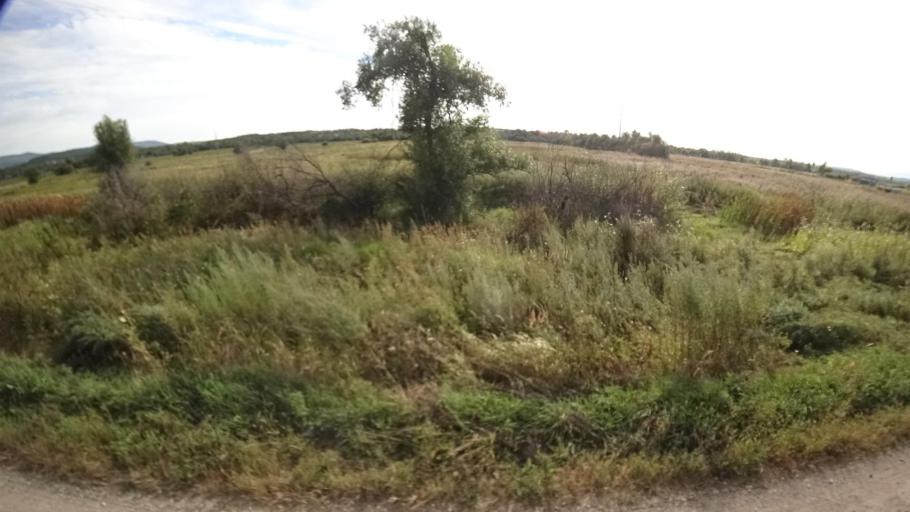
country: RU
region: Primorskiy
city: Dostoyevka
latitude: 44.3130
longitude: 133.4606
